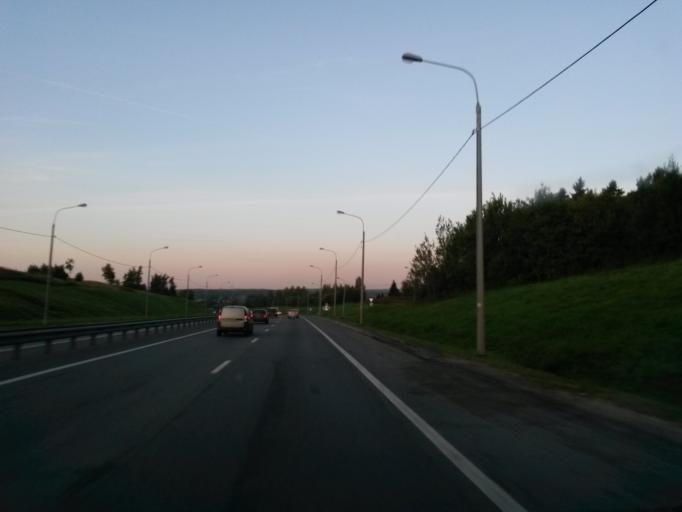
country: RU
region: Moskovskaya
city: Sergiyev Posad
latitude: 56.2871
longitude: 38.2113
